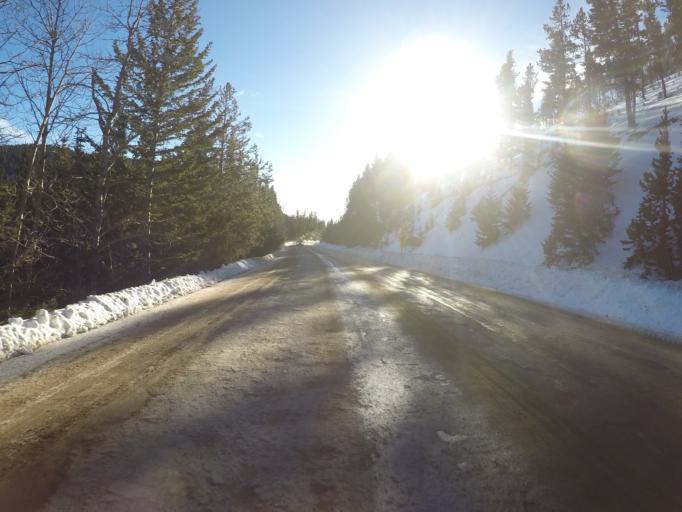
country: US
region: Montana
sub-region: Carbon County
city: Red Lodge
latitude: 45.1818
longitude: -109.3237
